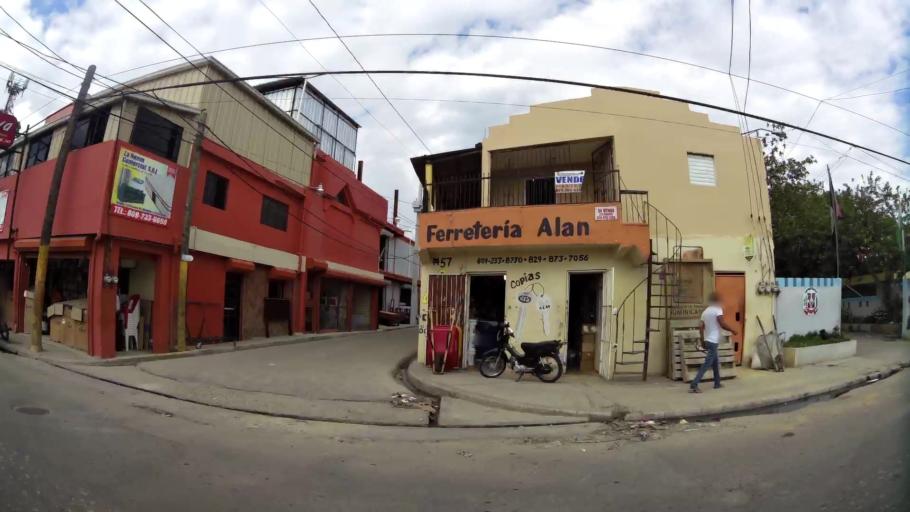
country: DO
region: Santiago
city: Santiago de los Caballeros
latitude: 19.4330
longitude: -70.7059
